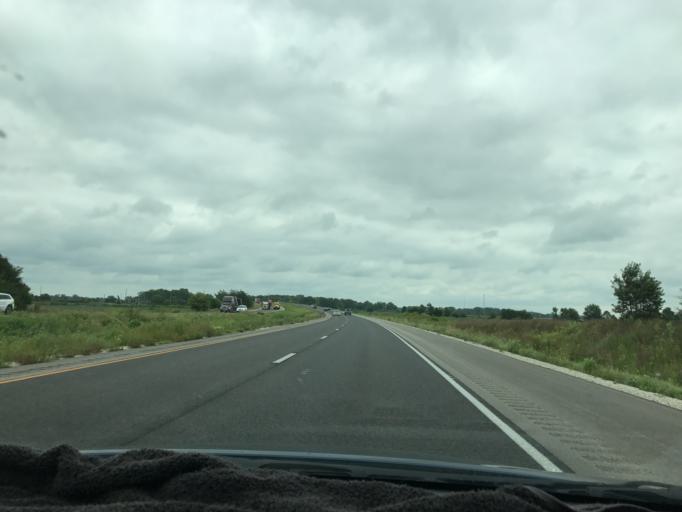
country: US
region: Illinois
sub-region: Henry County
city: Kewanee
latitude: 41.4061
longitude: -89.9733
